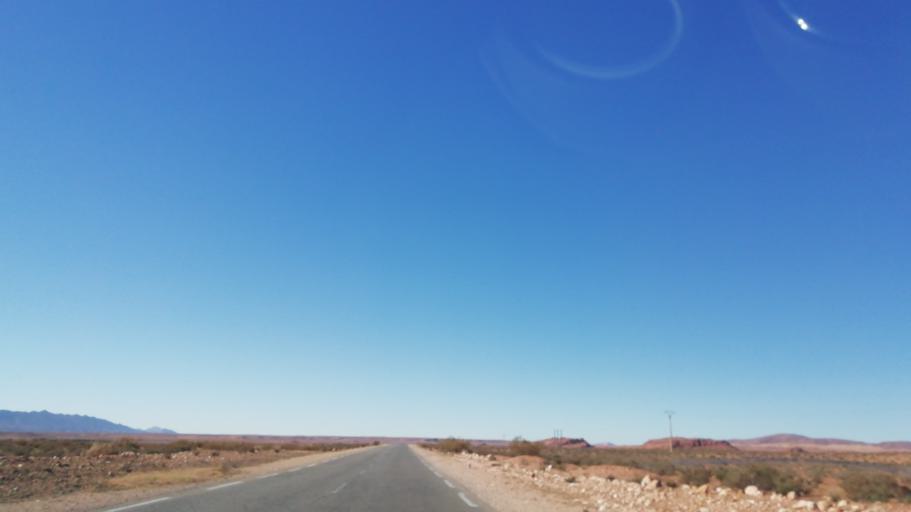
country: DZ
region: El Bayadh
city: El Abiodh Sidi Cheikh
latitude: 33.1804
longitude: 0.5455
